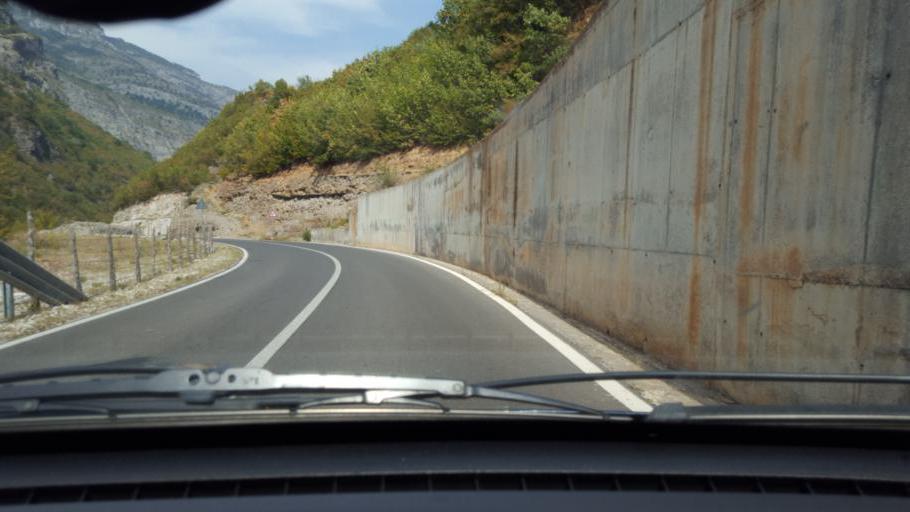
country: AL
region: Shkoder
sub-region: Rrethi i Malesia e Madhe
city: Kastrat
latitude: 42.4296
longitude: 19.5335
